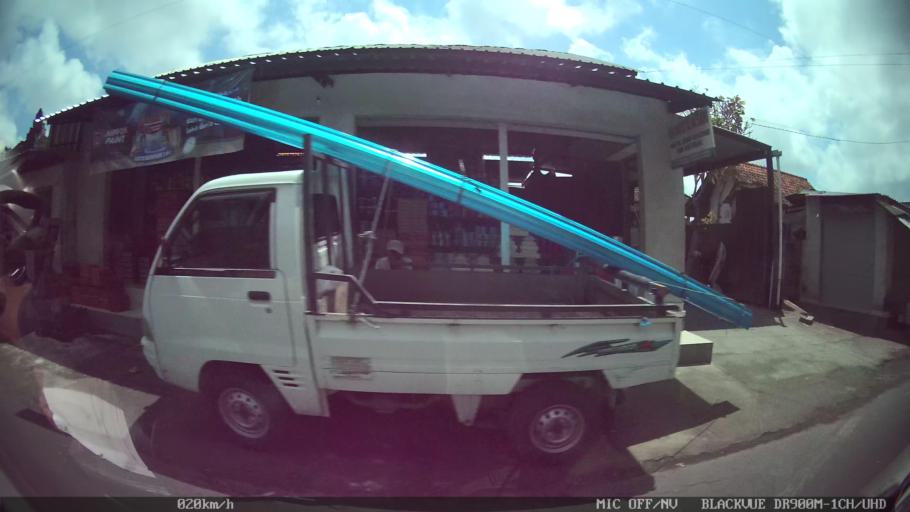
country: ID
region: Bali
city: Banjar Pasekan
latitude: -8.5923
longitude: 115.2848
